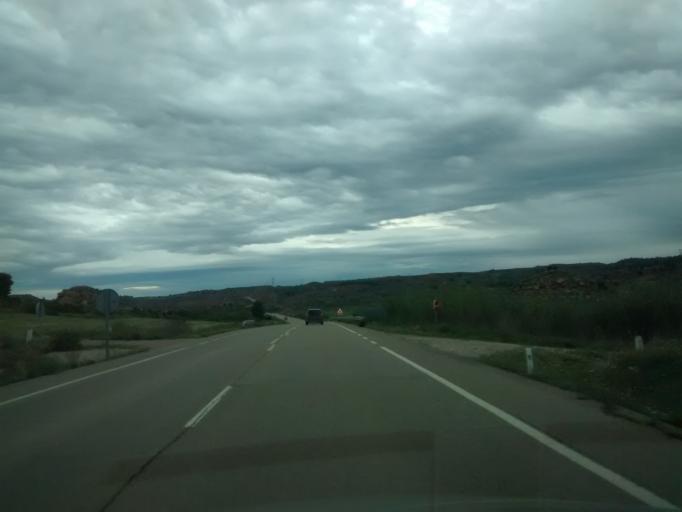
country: ES
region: Aragon
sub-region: Provincia de Zaragoza
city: Caspe
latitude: 41.1852
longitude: 0.0486
